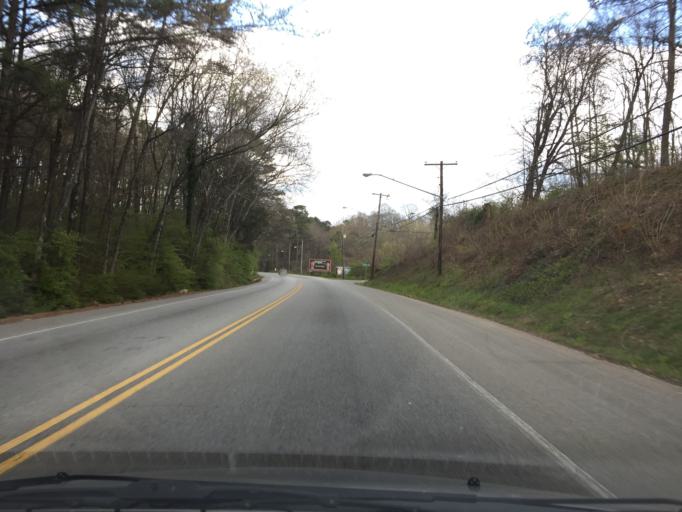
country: US
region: Tennessee
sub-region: Hamilton County
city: East Chattanooga
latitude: 35.0742
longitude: -85.2342
